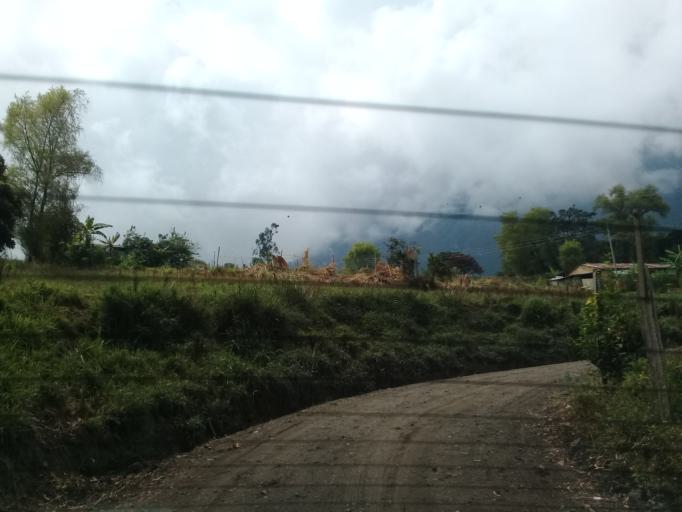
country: CO
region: Cundinamarca
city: Caqueza
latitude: 4.4101
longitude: -73.9861
